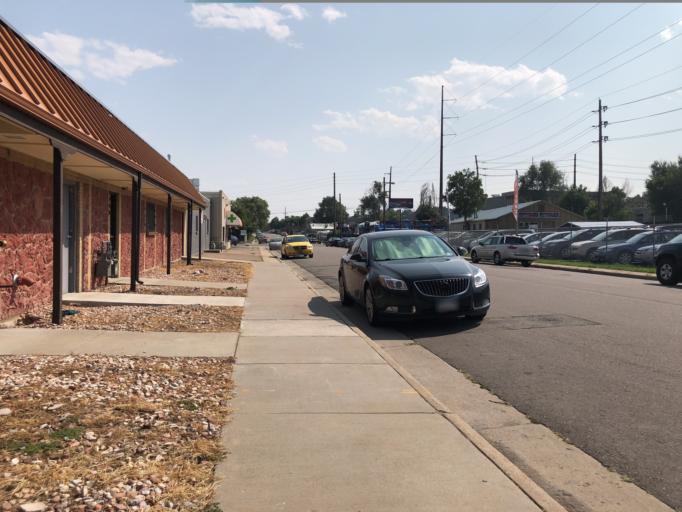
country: US
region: Colorado
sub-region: Denver County
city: Denver
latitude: 39.6957
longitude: -105.0003
